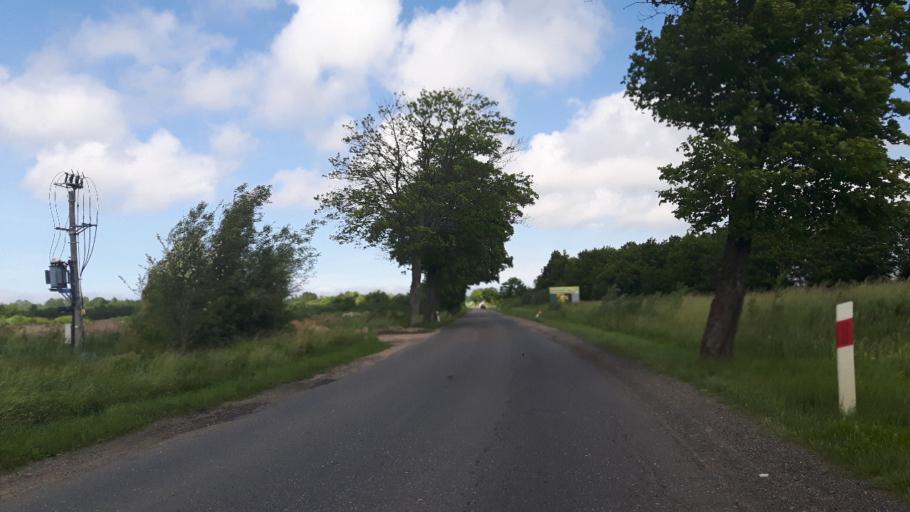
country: PL
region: Pomeranian Voivodeship
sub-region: Powiat slupski
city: Ustka
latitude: 54.5506
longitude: 16.8344
